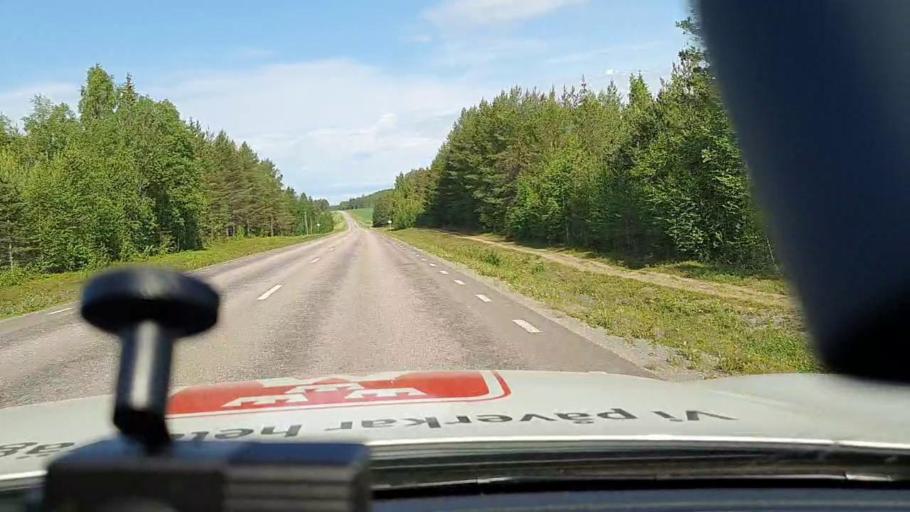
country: SE
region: Norrbotten
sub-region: Bodens Kommun
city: Boden
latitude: 65.9086
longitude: 21.3554
